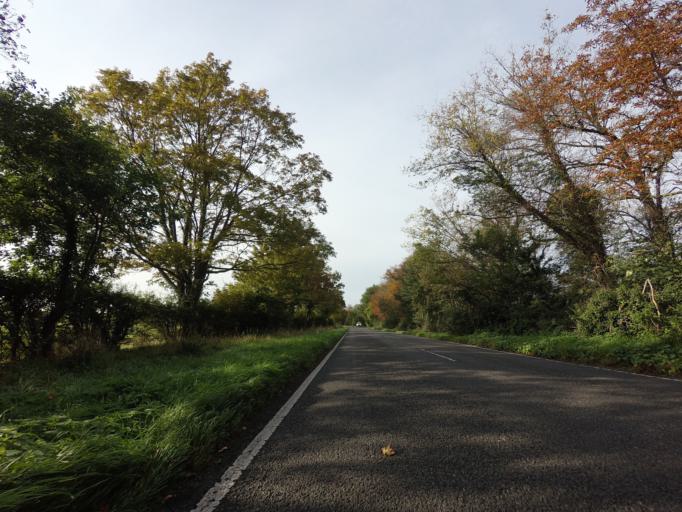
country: GB
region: England
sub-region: Cambridgeshire
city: Harston
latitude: 52.1123
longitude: 0.0929
